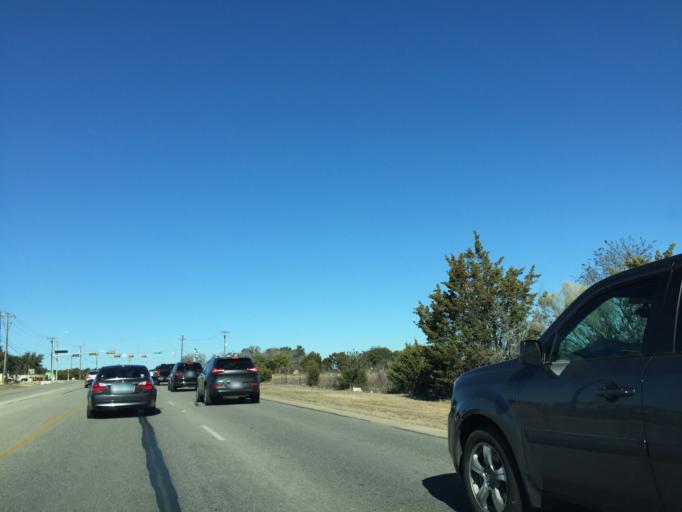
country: US
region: Texas
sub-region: Williamson County
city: Leander
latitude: 30.5676
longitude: -97.8670
